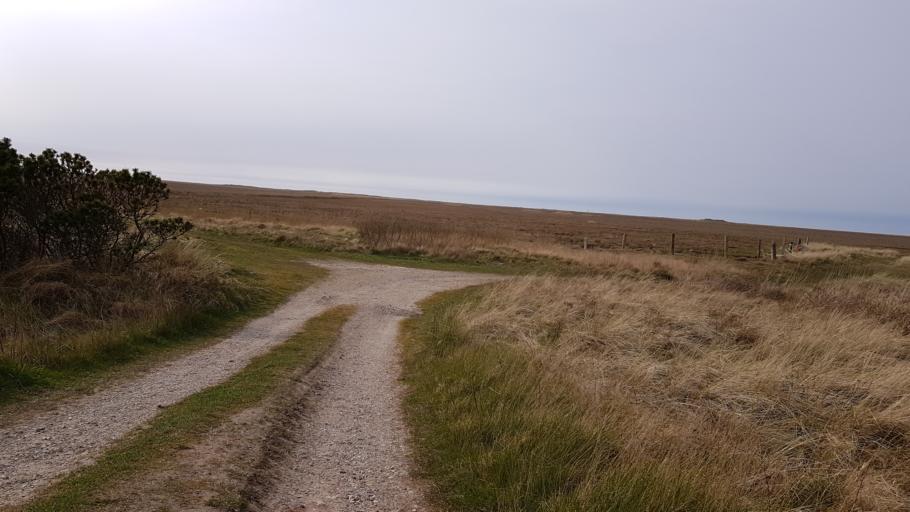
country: DE
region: Schleswig-Holstein
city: List
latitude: 55.1588
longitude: 8.5175
